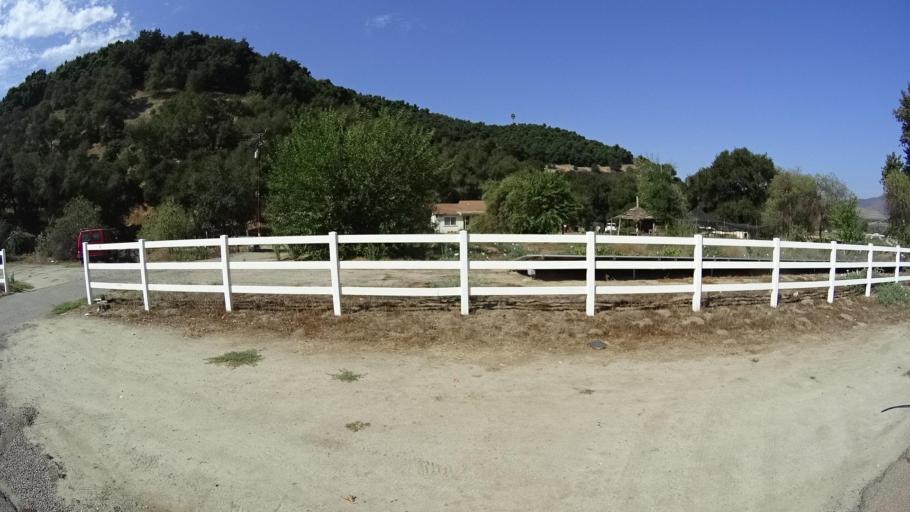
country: US
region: California
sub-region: San Diego County
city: Valley Center
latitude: 33.3075
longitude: -117.0015
